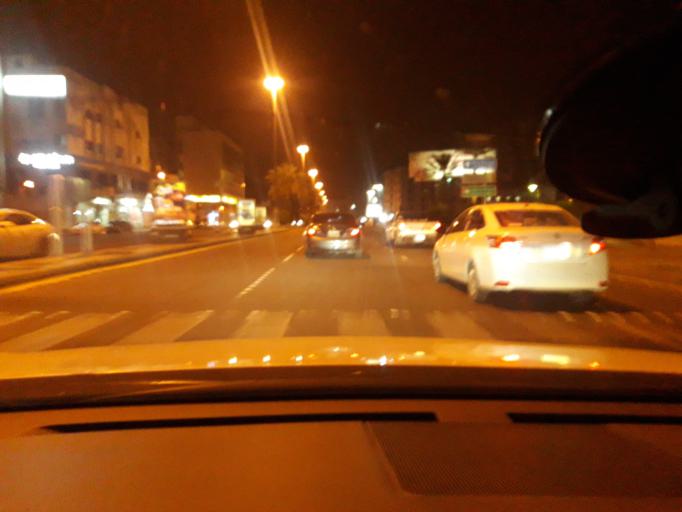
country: SA
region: Al Madinah al Munawwarah
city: Sultanah
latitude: 24.4831
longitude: 39.5972
